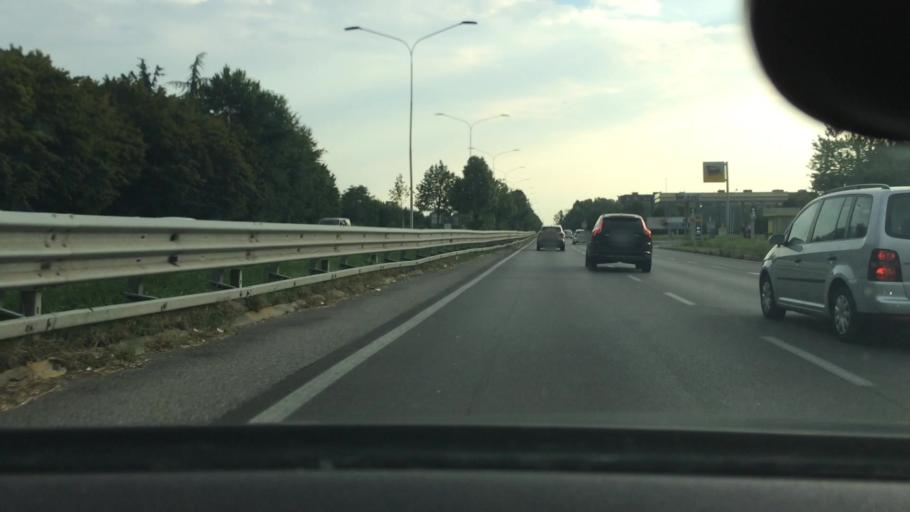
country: IT
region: Lombardy
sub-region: Provincia di Bergamo
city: Orio al Serio
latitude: 45.6868
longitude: 9.6861
